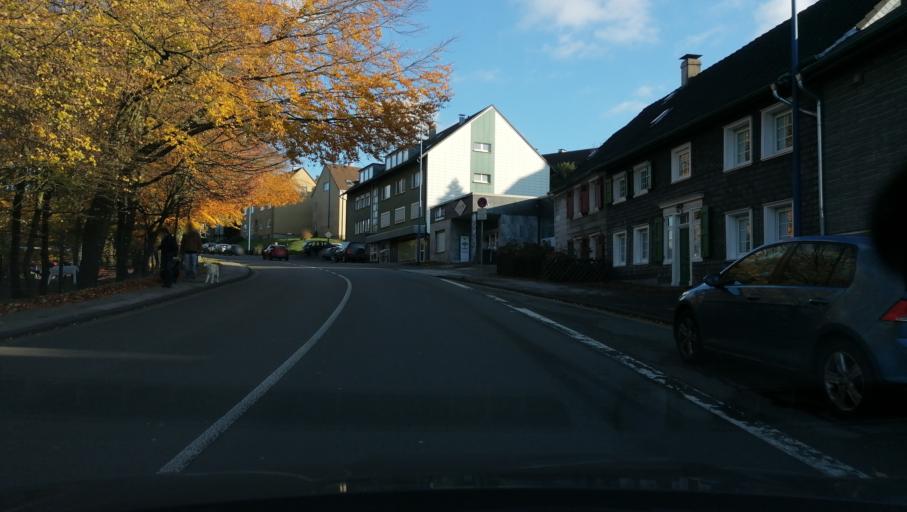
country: DE
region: North Rhine-Westphalia
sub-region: Regierungsbezirk Arnsberg
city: Schwelm
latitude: 51.2795
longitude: 7.2980
